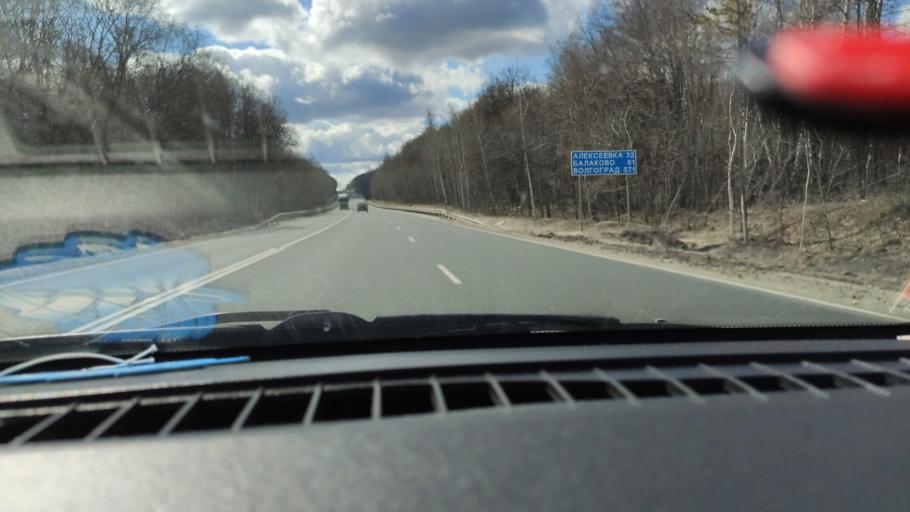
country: RU
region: Saratov
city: Khvalynsk
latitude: 52.5076
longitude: 48.0157
